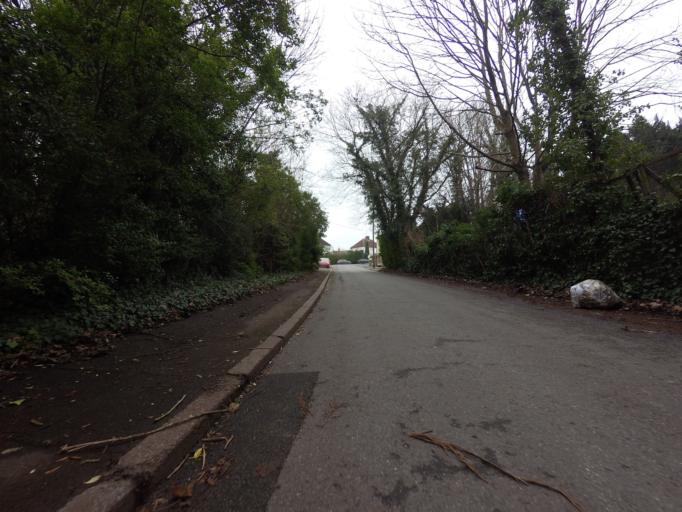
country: GB
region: England
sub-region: Kent
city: Eynsford
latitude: 51.3859
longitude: 0.2427
